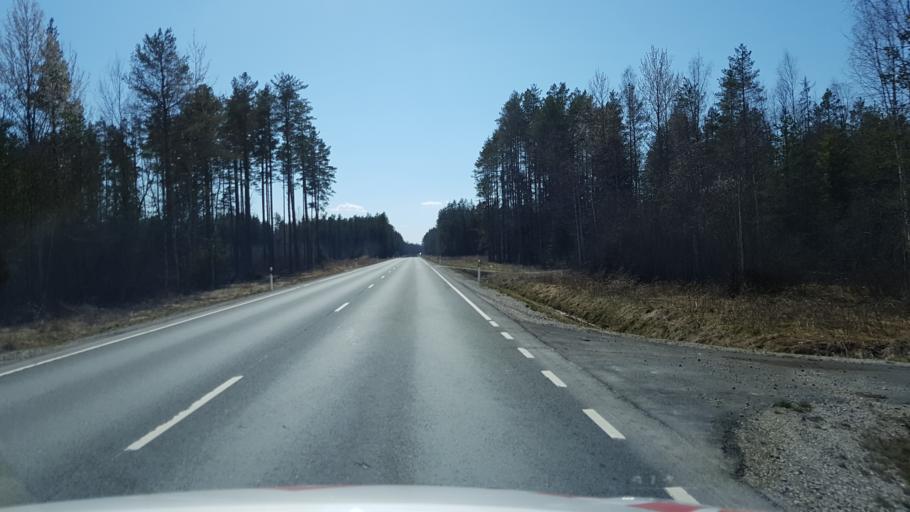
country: EE
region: Jogevamaa
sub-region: Mustvee linn
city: Mustvee
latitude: 58.8781
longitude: 26.9497
